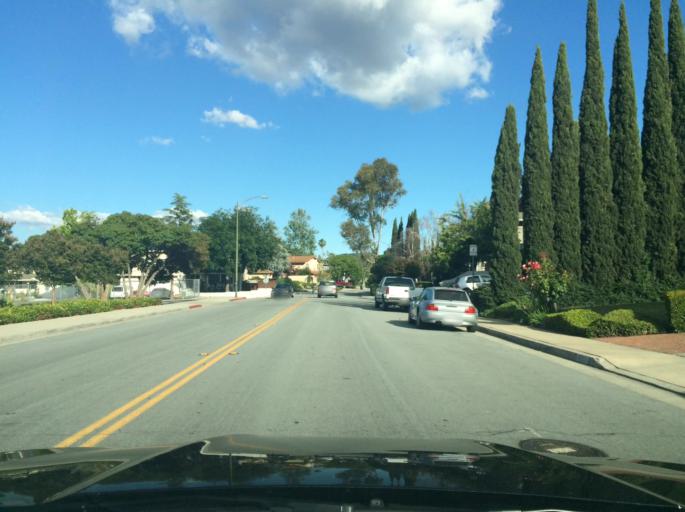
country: US
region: California
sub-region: Santa Clara County
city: Cambrian Park
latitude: 37.2187
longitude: -121.8790
